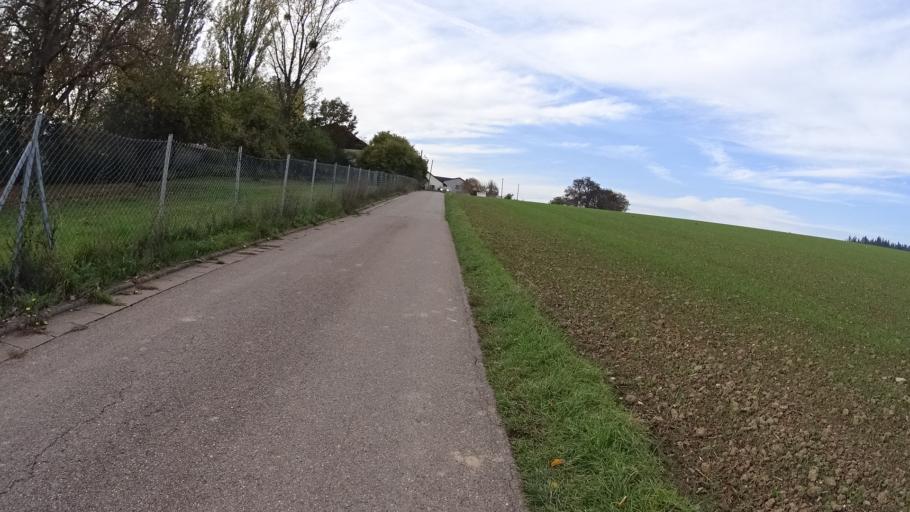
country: DE
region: Bavaria
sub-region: Upper Bavaria
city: Buxheim
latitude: 48.8296
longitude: 11.2740
